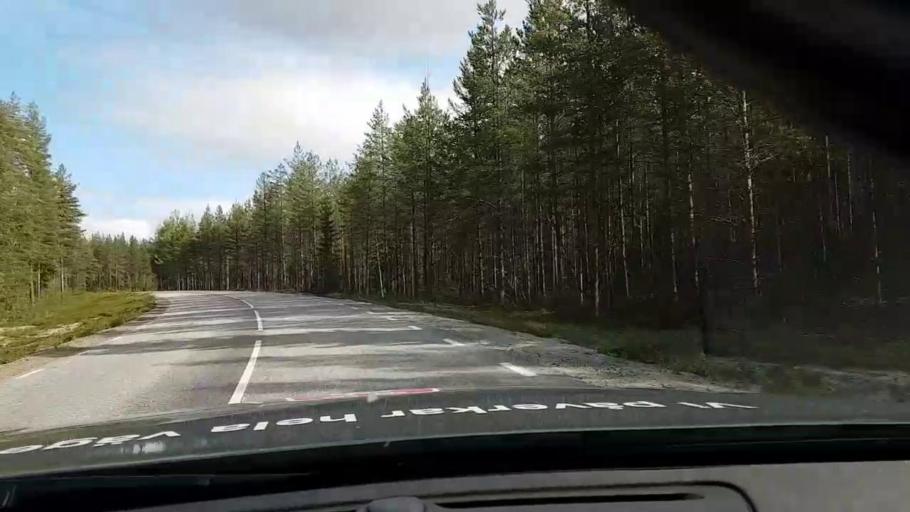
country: SE
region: Vaesternorrland
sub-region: OErnskoeldsviks Kommun
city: Bredbyn
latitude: 63.6543
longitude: 17.8779
